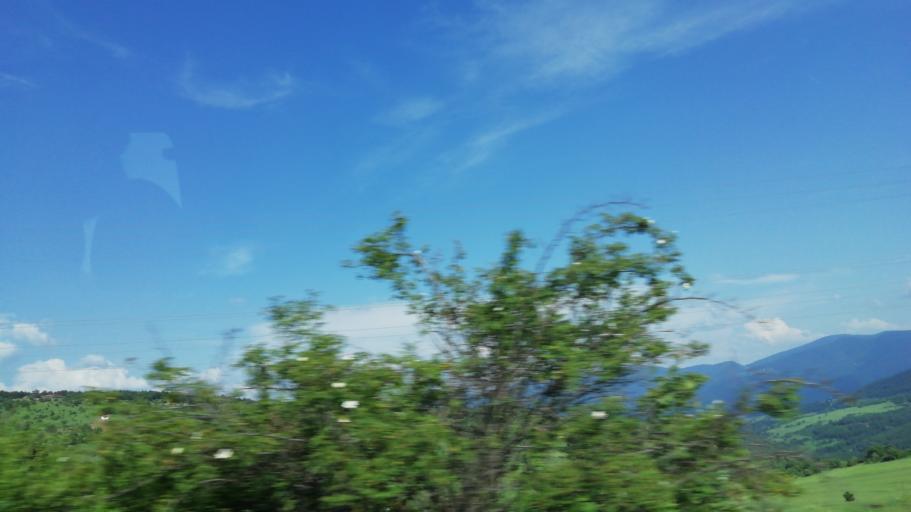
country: TR
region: Karabuk
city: Karabuk
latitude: 41.1034
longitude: 32.5951
